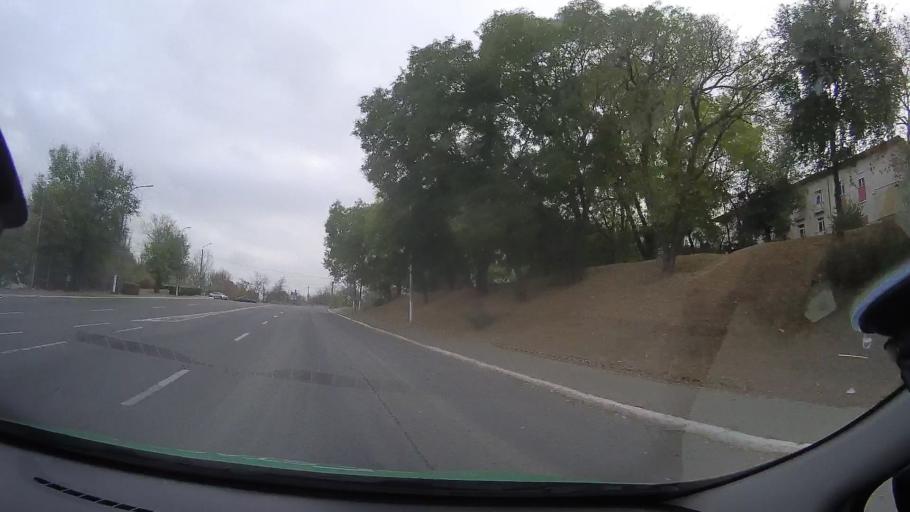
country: RO
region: Constanta
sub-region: Municipiul Medgidia
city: Medgidia
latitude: 44.2453
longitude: 28.2597
